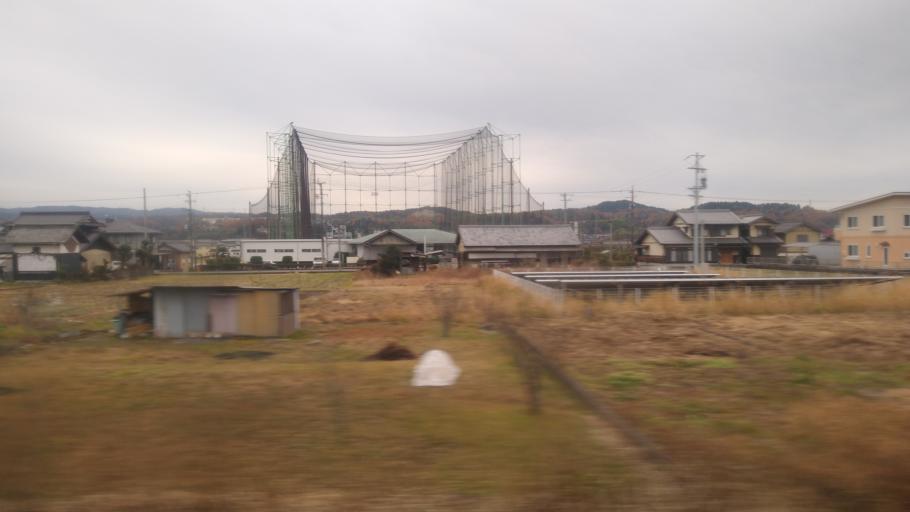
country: JP
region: Gifu
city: Toki
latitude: 35.3672
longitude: 137.2064
